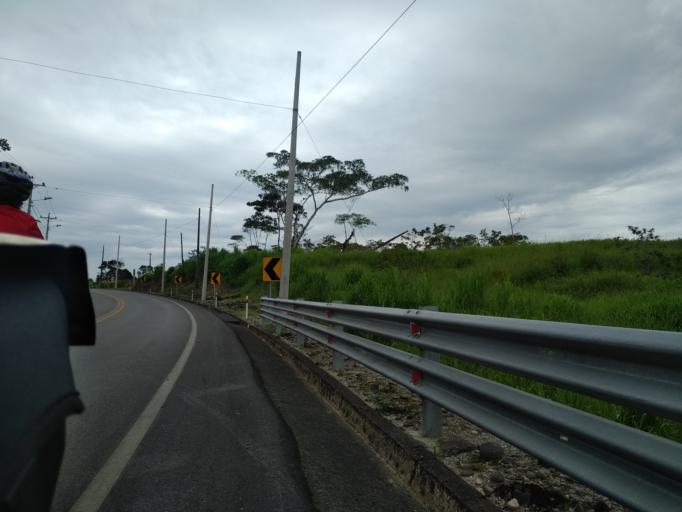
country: EC
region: Napo
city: Tena
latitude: -1.2056
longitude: -77.8745
